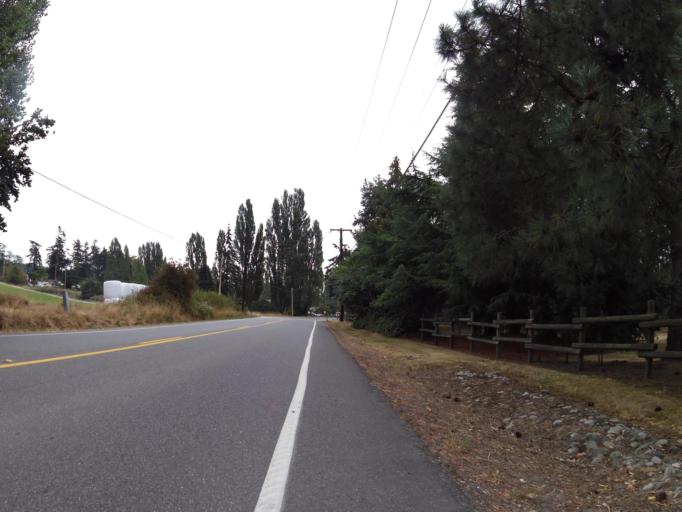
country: US
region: Washington
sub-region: Island County
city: Coupeville
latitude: 48.2001
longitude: -122.6697
